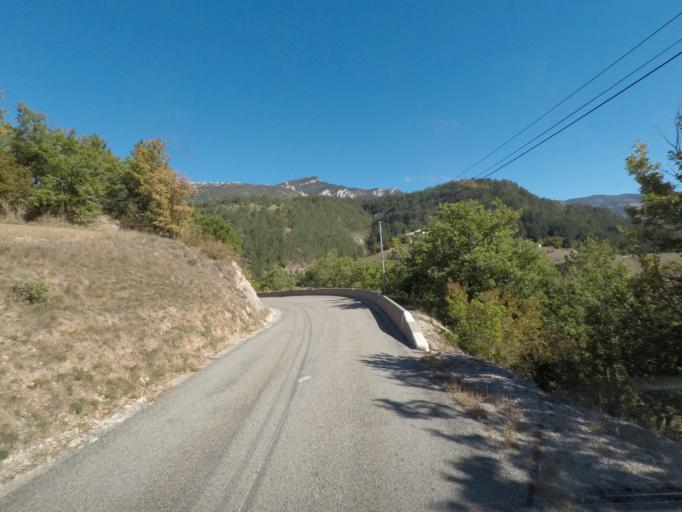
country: FR
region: Rhone-Alpes
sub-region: Departement de la Drome
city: Die
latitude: 44.6232
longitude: 5.3063
